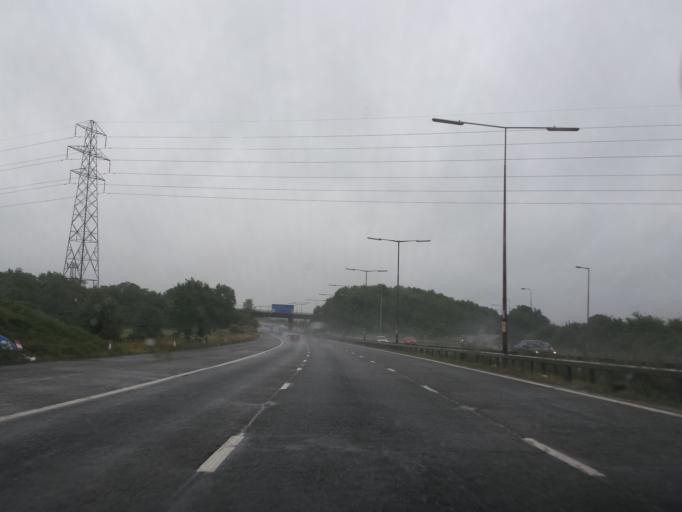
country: GB
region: England
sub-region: Warwickshire
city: Bedworth
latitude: 52.4441
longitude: -1.4254
